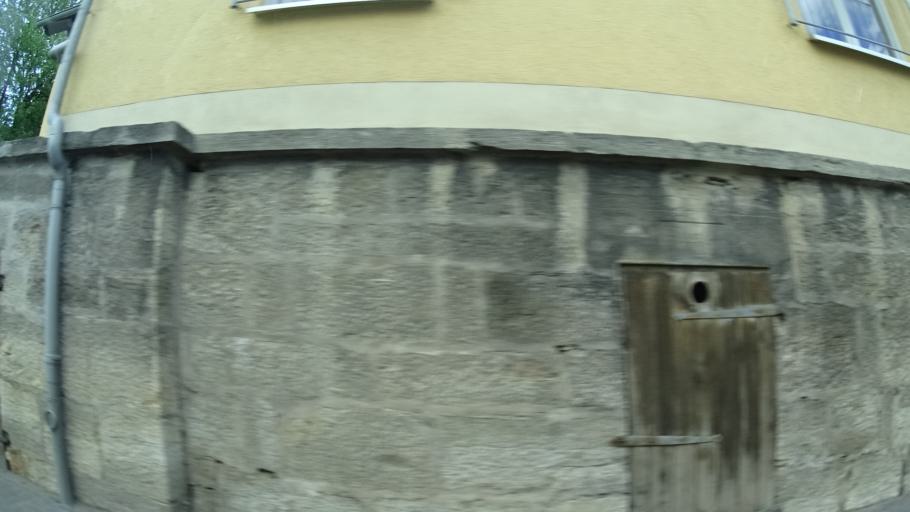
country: DE
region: Thuringia
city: Belrieth
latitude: 50.5269
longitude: 10.4943
